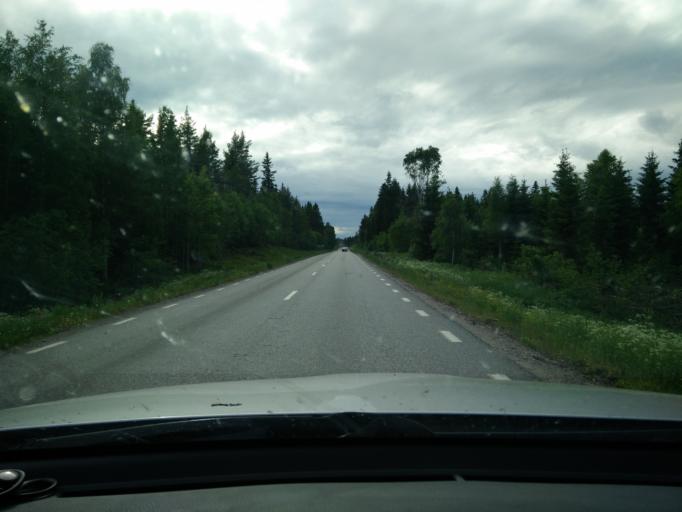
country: SE
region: Gaevleborg
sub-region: Nordanstigs Kommun
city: Bergsjoe
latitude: 62.0975
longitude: 16.7557
